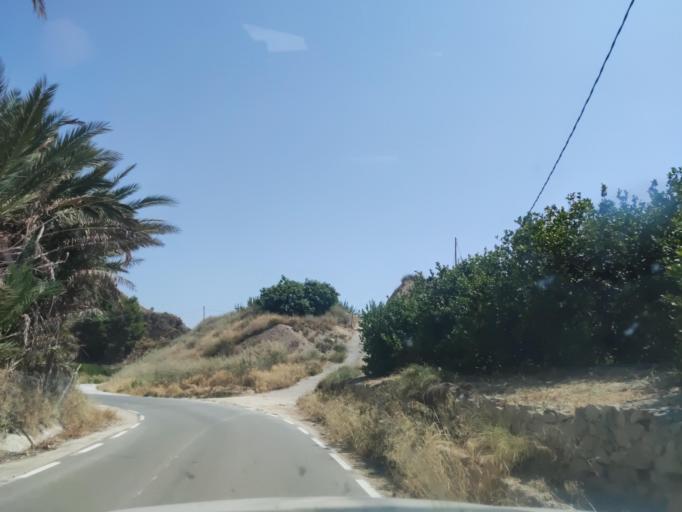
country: ES
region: Murcia
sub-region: Murcia
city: Ulea
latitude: 38.1326
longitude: -1.3141
